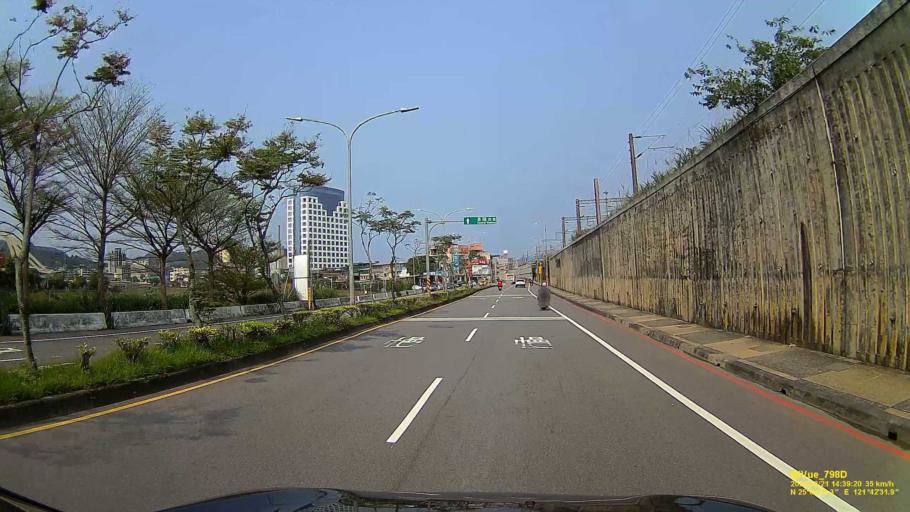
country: TW
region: Taiwan
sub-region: Keelung
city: Keelung
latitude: 25.0916
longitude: 121.7090
